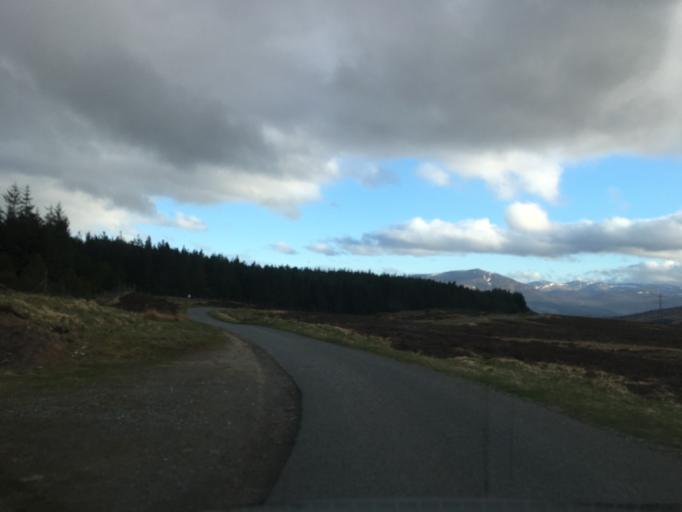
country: GB
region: Scotland
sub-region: Perth and Kinross
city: Aberfeldy
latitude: 56.7759
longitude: -4.0834
